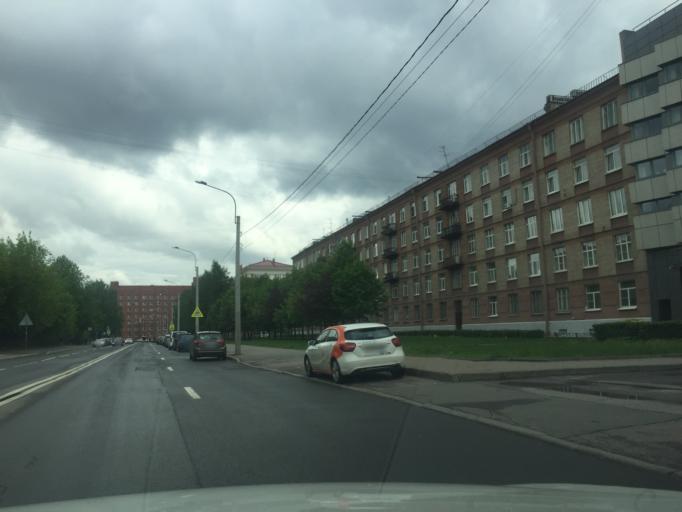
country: RU
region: St.-Petersburg
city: Vasyl'evsky Ostrov
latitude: 59.9343
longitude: 30.2497
